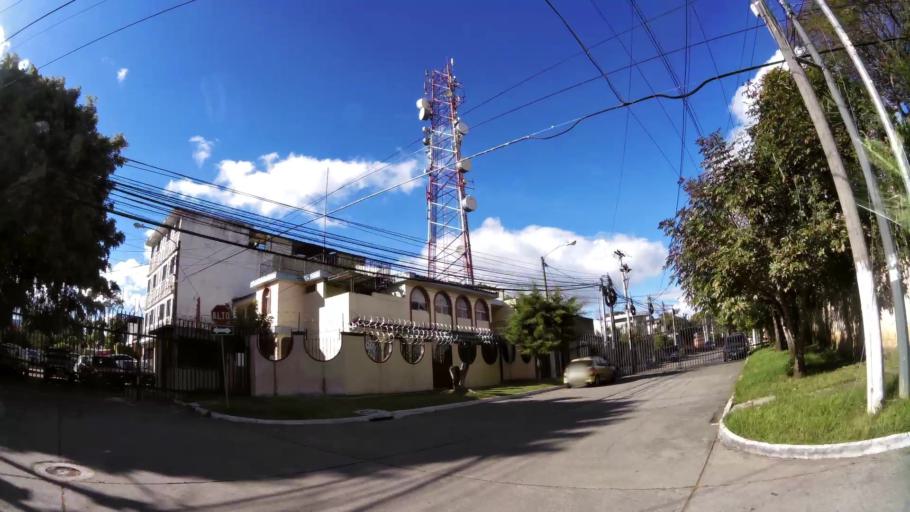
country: GT
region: Guatemala
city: Guatemala City
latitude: 14.6051
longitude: -90.5535
